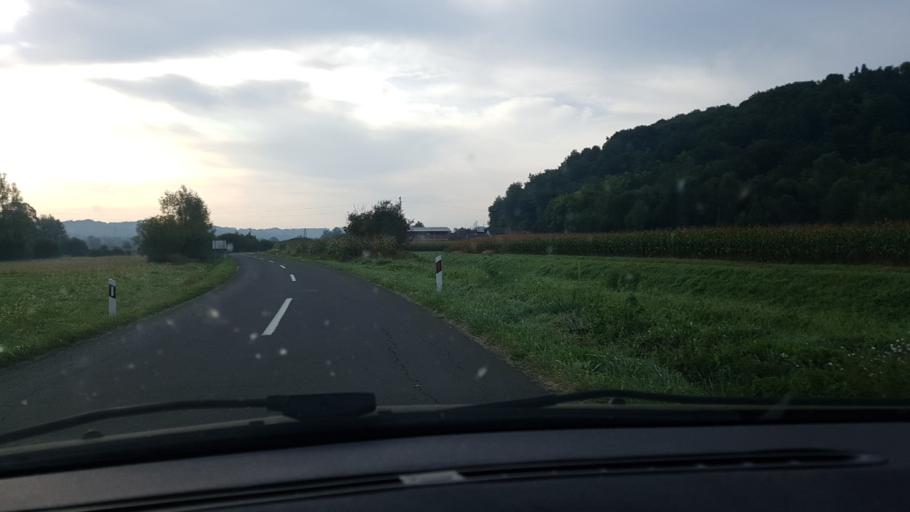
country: HR
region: Krapinsko-Zagorska
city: Zlatar
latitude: 46.1037
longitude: 16.0192
